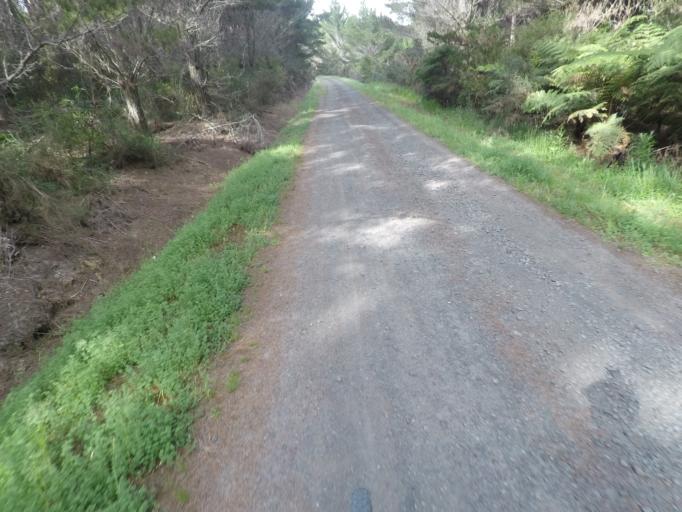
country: NZ
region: Auckland
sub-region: Auckland
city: Muriwai Beach
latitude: -36.7407
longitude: 174.5727
